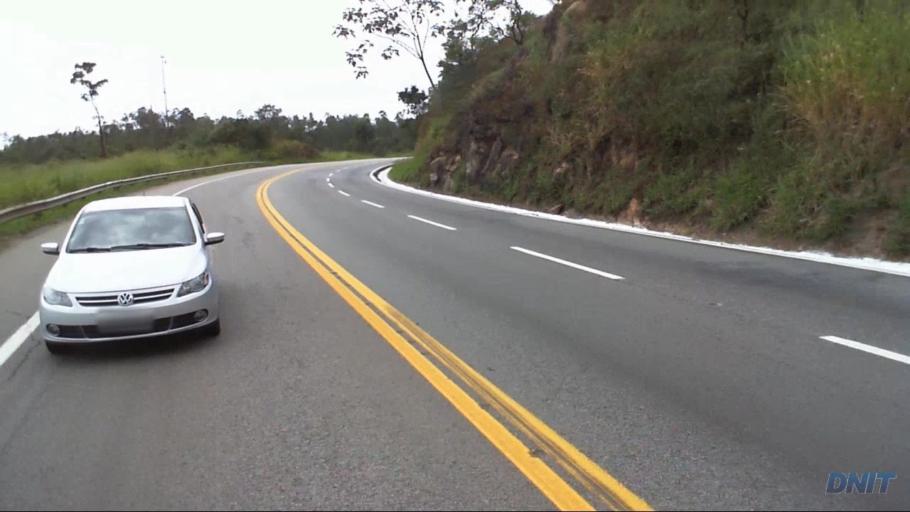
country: BR
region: Minas Gerais
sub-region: Caete
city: Caete
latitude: -19.7882
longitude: -43.7036
